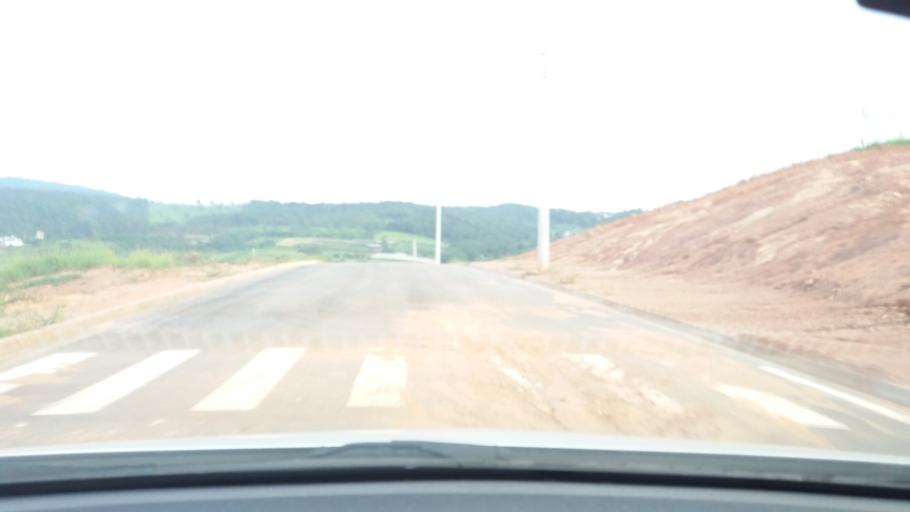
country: BR
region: Sao Paulo
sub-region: Bom Jesus Dos Perdoes
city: Bom Jesus dos Perdoes
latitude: -23.1534
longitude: -46.4747
